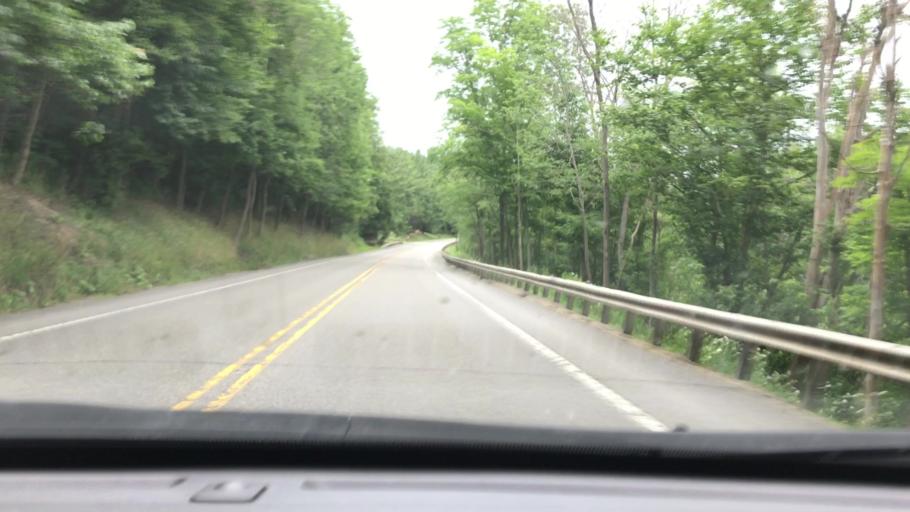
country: US
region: Pennsylvania
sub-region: McKean County
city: Bradford
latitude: 41.8578
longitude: -78.6733
